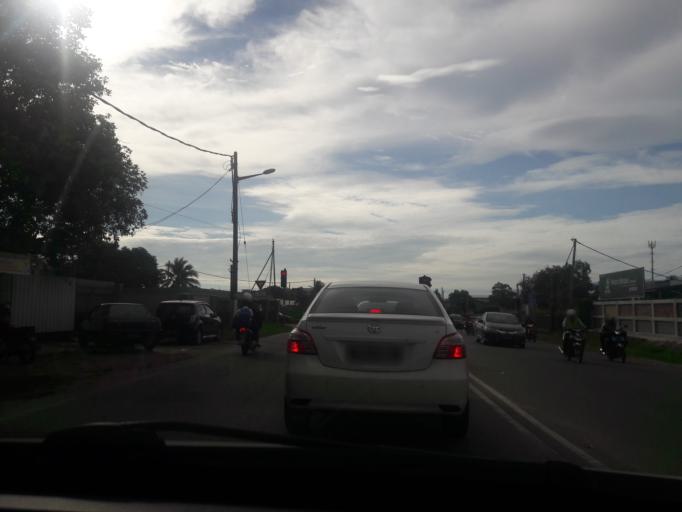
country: MY
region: Kedah
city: Sungai Petani
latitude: 5.6334
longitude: 100.5170
